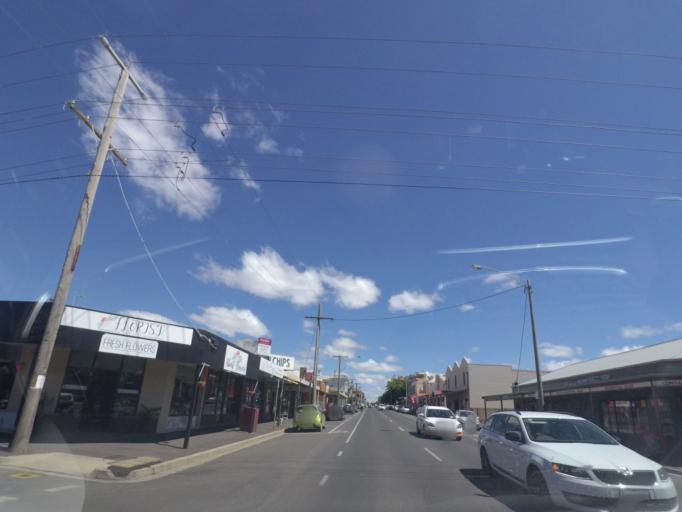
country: AU
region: Victoria
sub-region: Mount Alexander
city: Castlemaine
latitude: -37.2457
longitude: 144.4539
